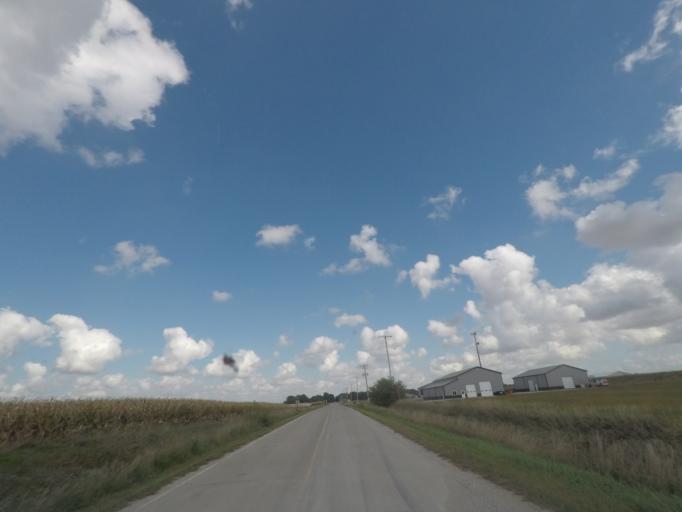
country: US
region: Iowa
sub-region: Story County
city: Nevada
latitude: 42.0043
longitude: -93.3192
